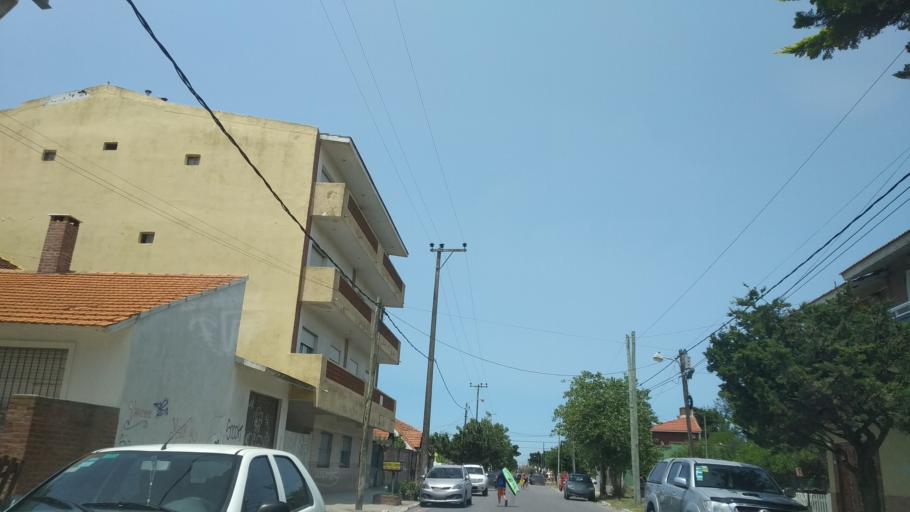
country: AR
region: Buenos Aires
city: Mar del Tuyu
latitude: -36.5592
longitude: -56.6895
